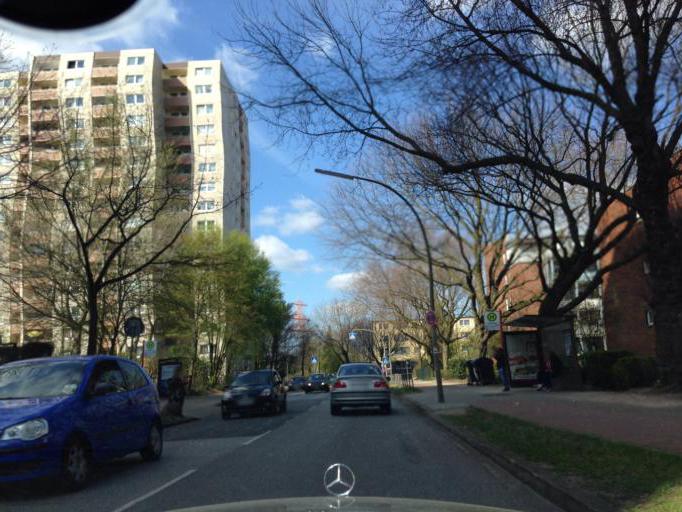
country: DE
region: Hamburg
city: Wandsbek
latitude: 53.5623
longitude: 10.1086
